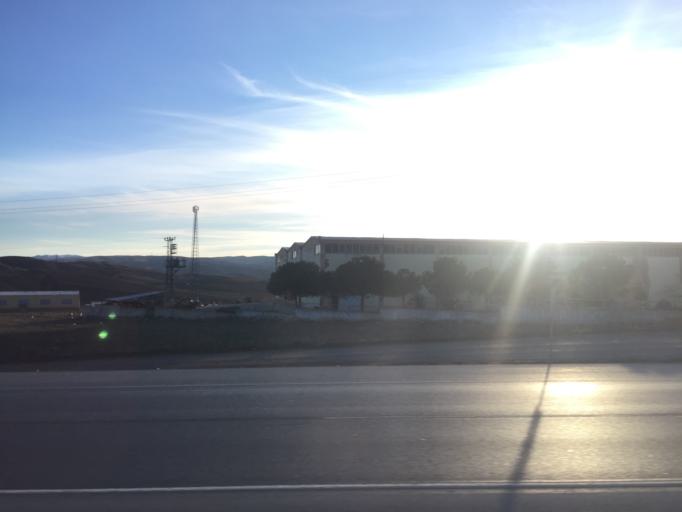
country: TR
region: Kirikkale
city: Yahsihan
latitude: 39.8819
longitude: 33.4371
